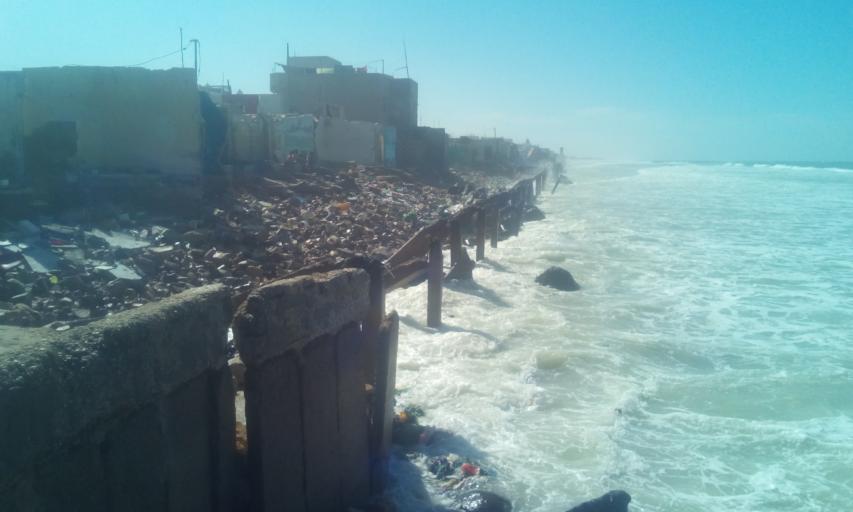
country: SN
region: Saint-Louis
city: Saint-Louis
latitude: 16.0259
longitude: -16.5093
